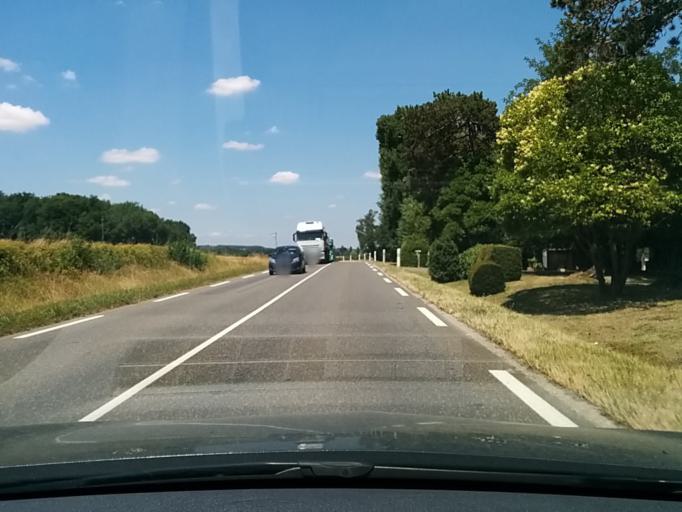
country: FR
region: Midi-Pyrenees
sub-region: Departement du Gers
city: Vic-Fezensac
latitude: 43.7312
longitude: 0.3751
